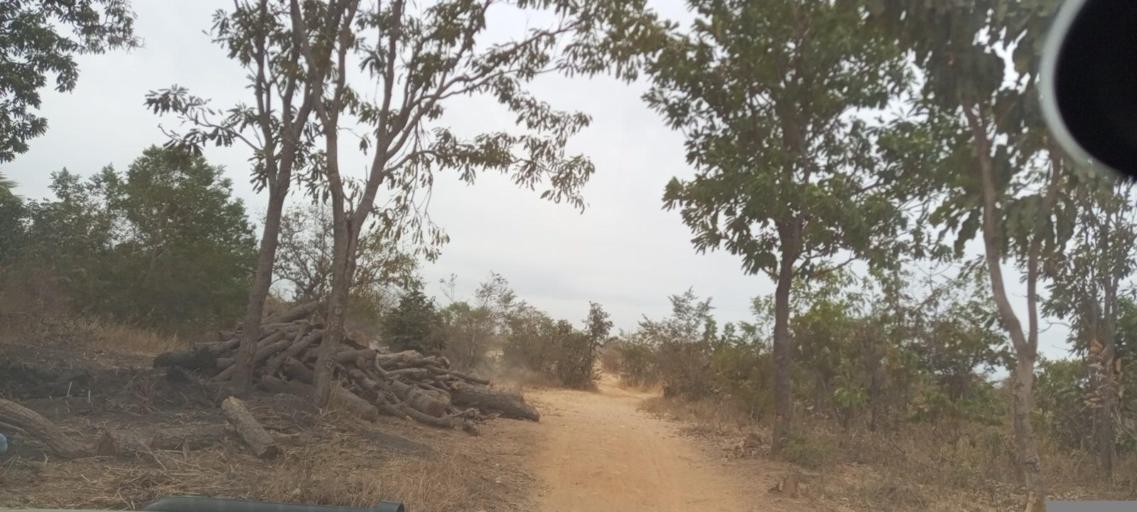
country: ML
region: Koulikoro
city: Kati
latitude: 12.7705
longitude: -8.3763
